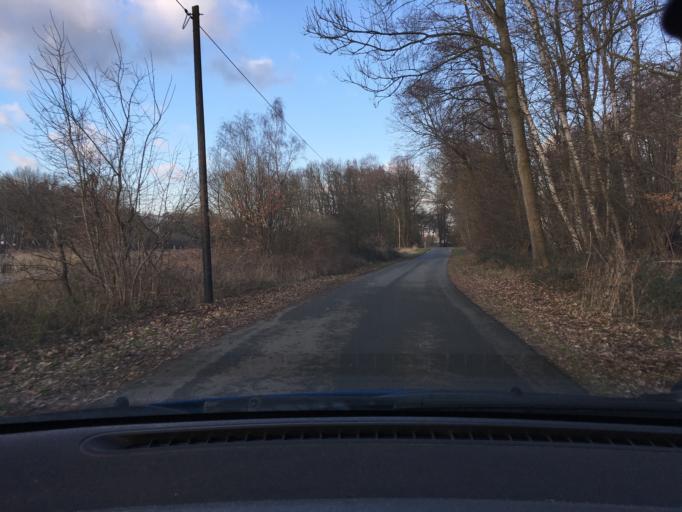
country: DE
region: Schleswig-Holstein
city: Witzeeze
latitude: 53.4582
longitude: 10.6262
